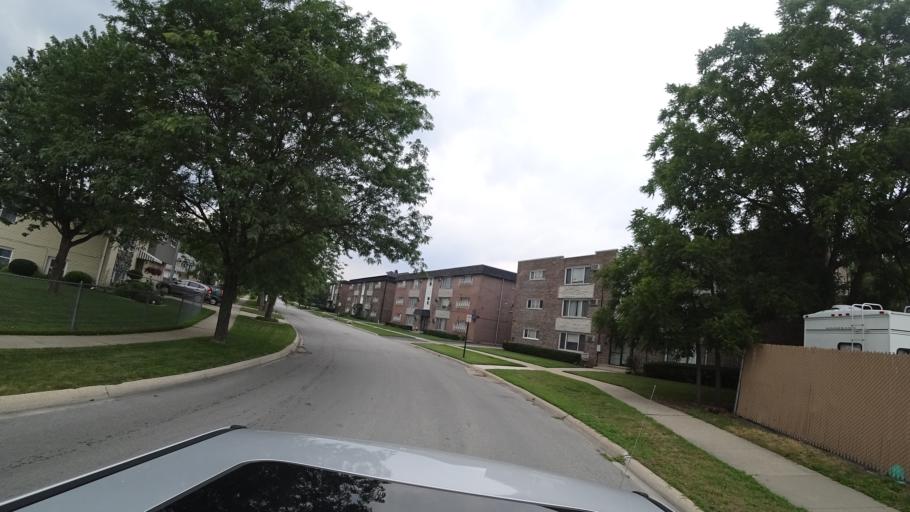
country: US
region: Illinois
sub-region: Cook County
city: Oak Lawn
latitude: 41.6959
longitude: -87.7621
